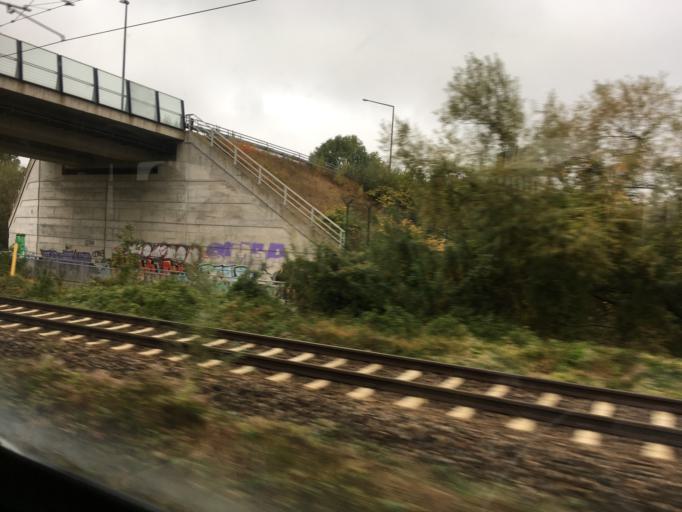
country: DE
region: Lower Saxony
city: Osnabrueck
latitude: 52.2690
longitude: 8.0848
